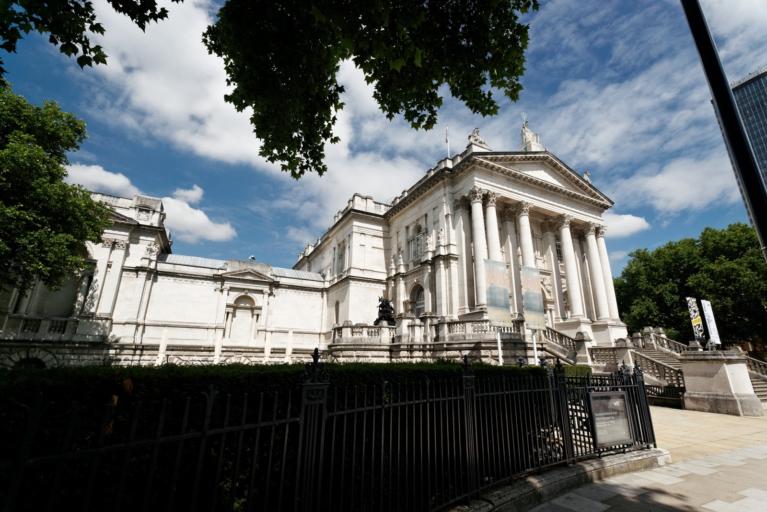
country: GB
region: England
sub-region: Greater London
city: City of Westminster
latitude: 51.4905
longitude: -0.1268
